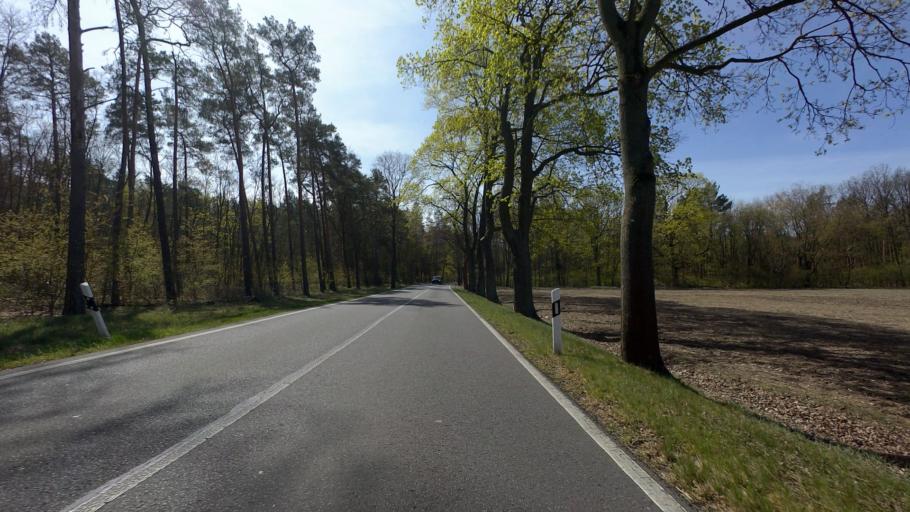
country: DE
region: Brandenburg
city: Trebbin
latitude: 52.2687
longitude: 13.2090
